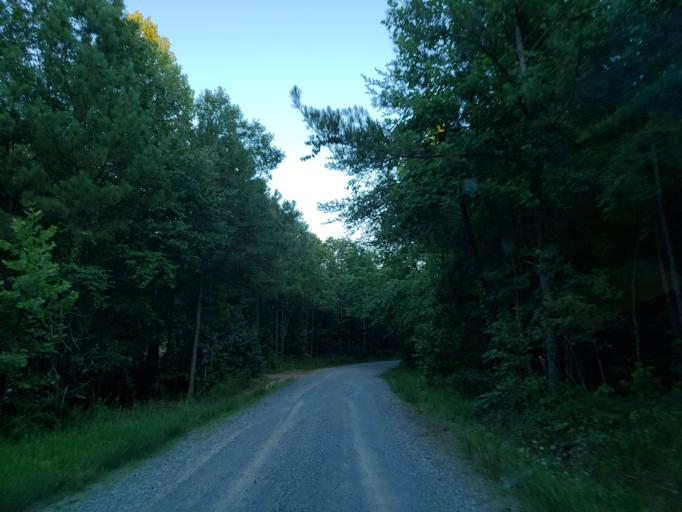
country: US
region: Georgia
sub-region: Bartow County
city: Euharlee
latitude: 34.0713
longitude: -84.8591
